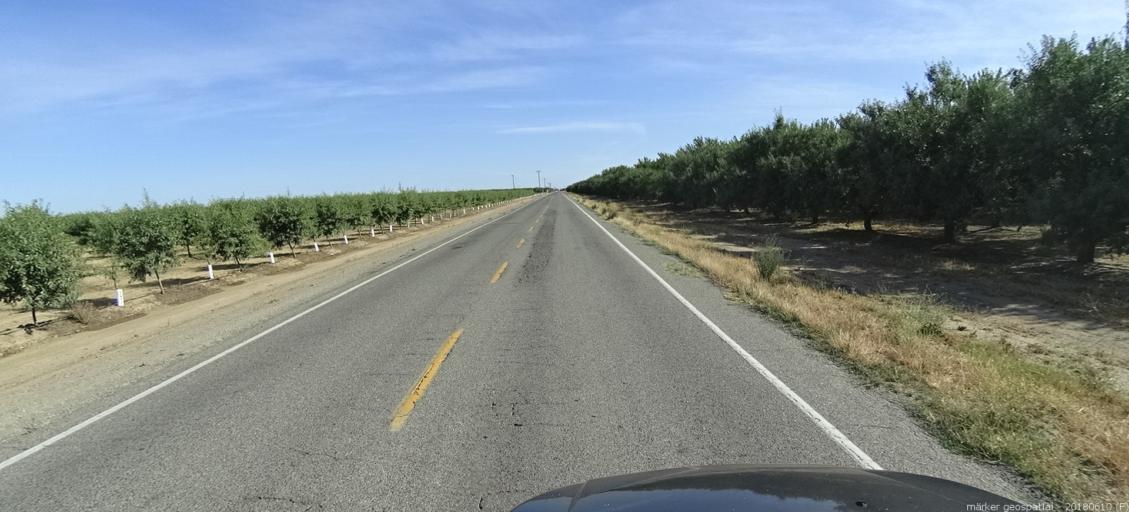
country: US
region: California
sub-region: Madera County
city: Fairmead
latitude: 37.0123
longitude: -120.2569
